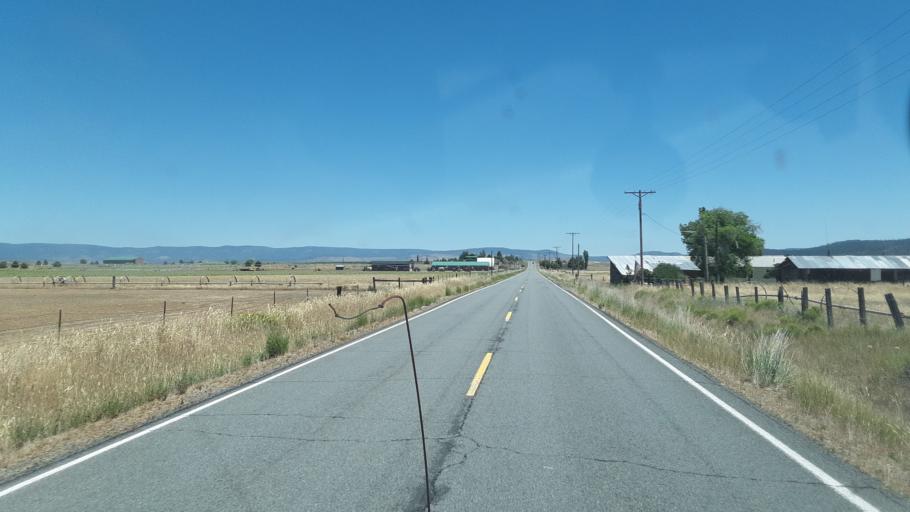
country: US
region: California
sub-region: Shasta County
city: Burney
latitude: 41.1321
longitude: -121.0778
